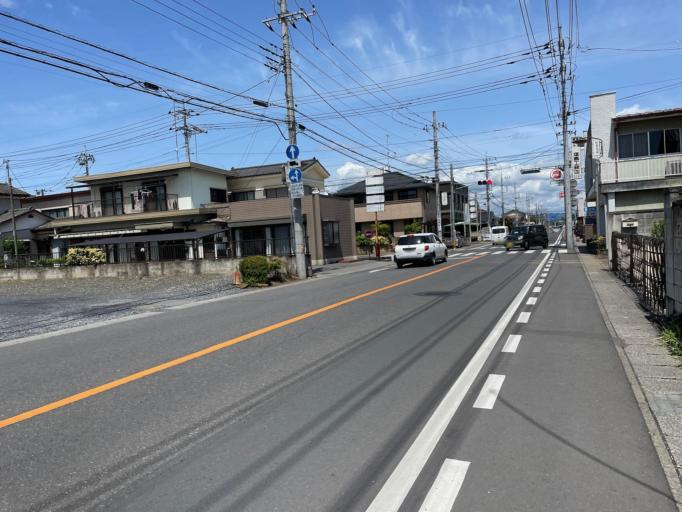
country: JP
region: Tochigi
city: Sano
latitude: 36.3187
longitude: 139.5848
